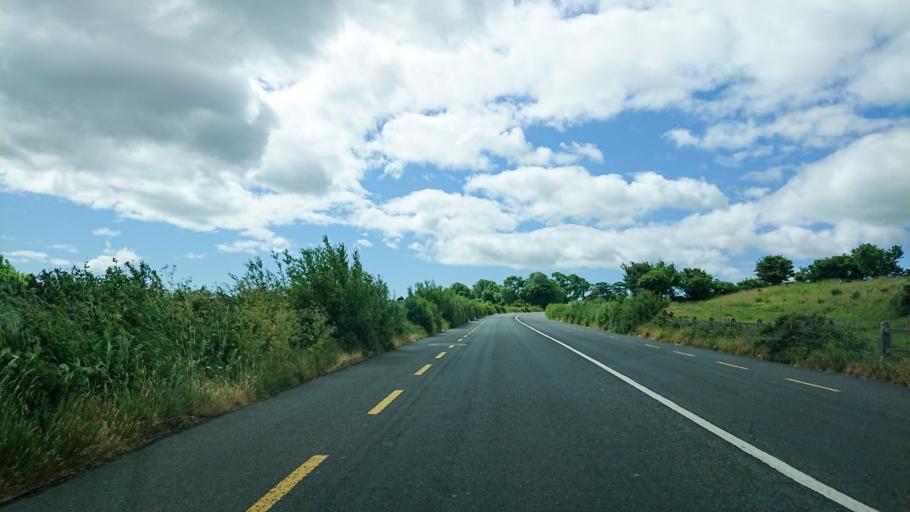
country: IE
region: Munster
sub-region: Waterford
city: Tra Mhor
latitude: 52.2118
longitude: -7.1937
